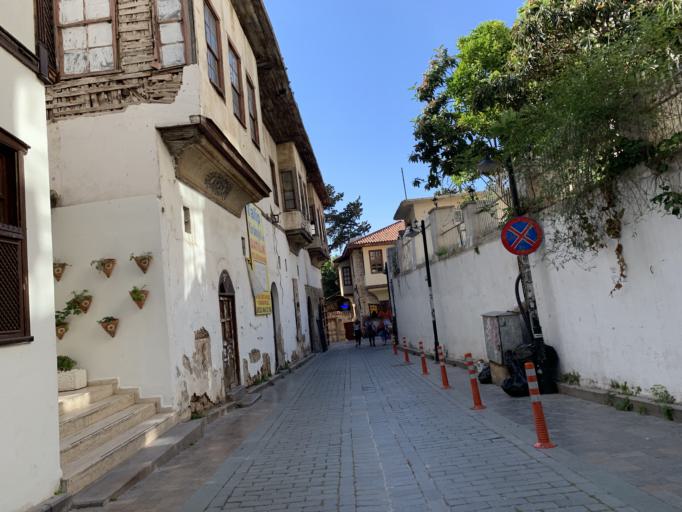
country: TR
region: Antalya
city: Antalya
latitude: 36.8848
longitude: 30.7053
